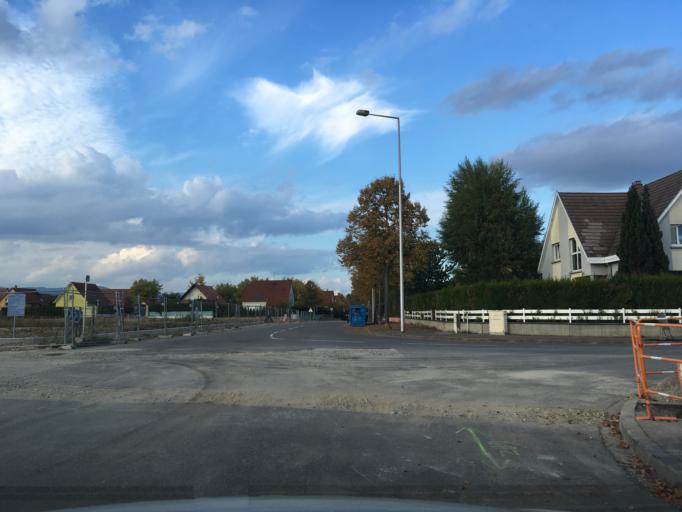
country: FR
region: Alsace
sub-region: Departement du Haut-Rhin
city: Wettolsheim
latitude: 48.0694
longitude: 7.3235
